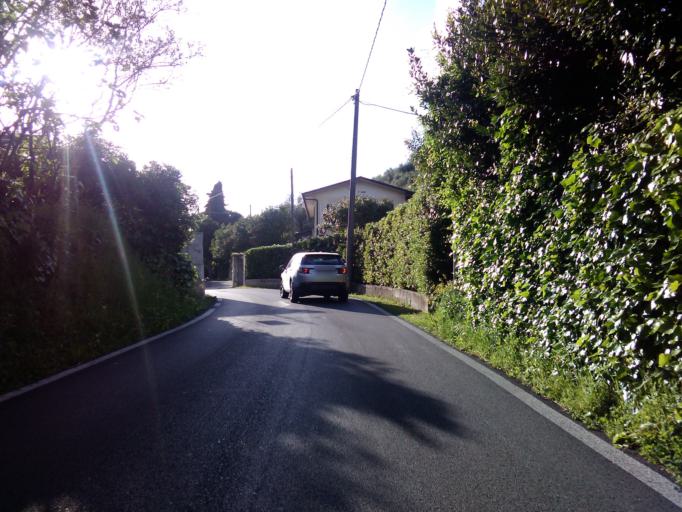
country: IT
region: Tuscany
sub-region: Provincia di Lucca
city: Camaiore
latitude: 43.9403
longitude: 10.2582
